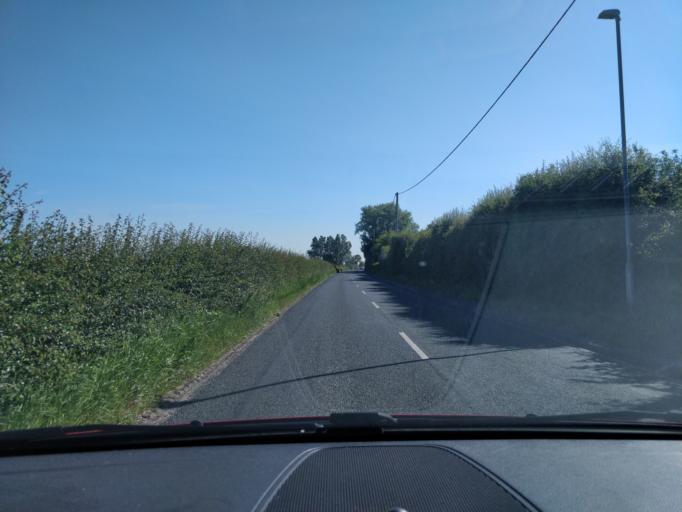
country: GB
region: England
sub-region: Lancashire
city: Banks
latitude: 53.6993
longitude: -2.8839
